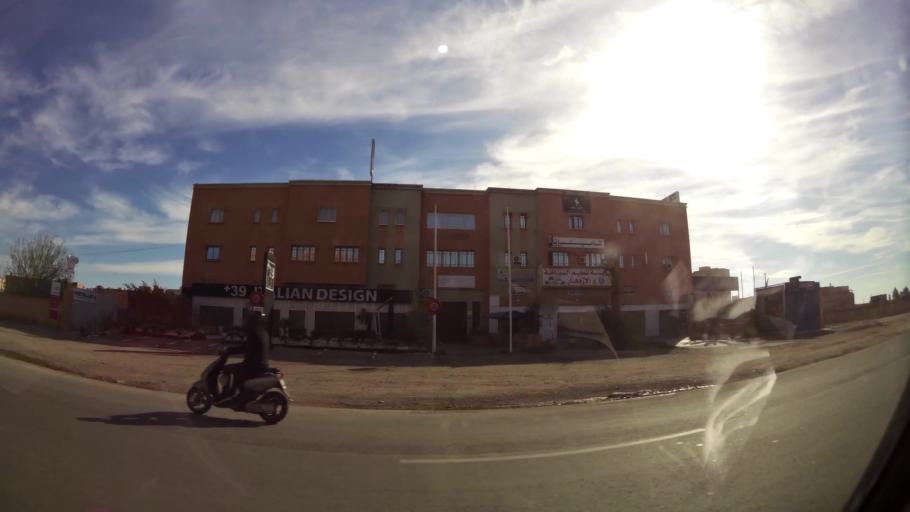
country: MA
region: Marrakech-Tensift-Al Haouz
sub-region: Marrakech
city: Marrakesh
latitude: 31.6641
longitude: -8.0321
